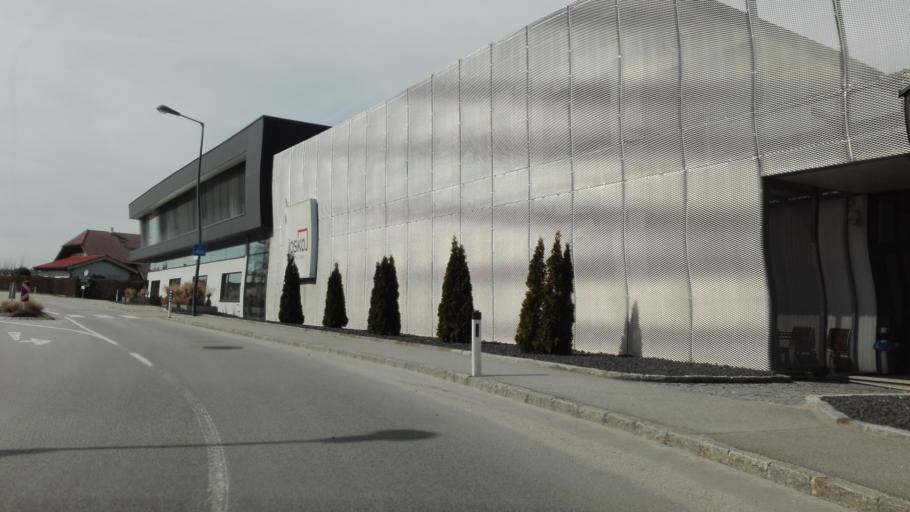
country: AT
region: Upper Austria
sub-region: Politischer Bezirk Scharding
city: Sankt Marienkirchen bei Schaerding
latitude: 48.3719
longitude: 13.5649
